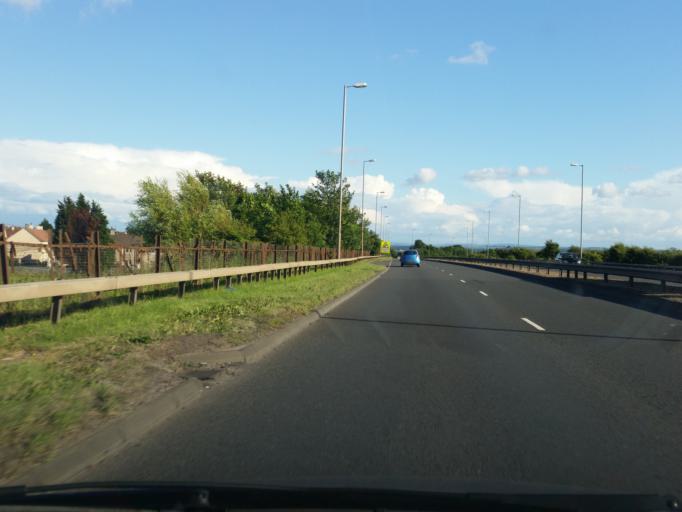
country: GB
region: Scotland
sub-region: North Lanarkshire
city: Bellshill
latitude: 55.8154
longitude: -4.0388
